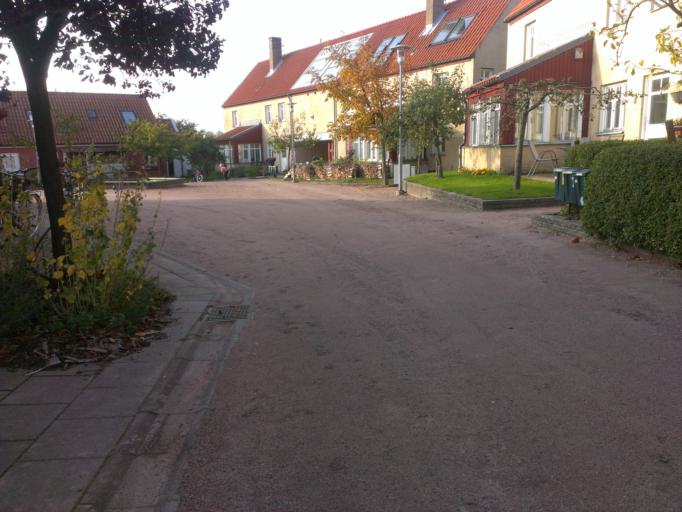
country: SE
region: Skane
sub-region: Malmo
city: Oxie
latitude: 55.5422
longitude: 13.1116
